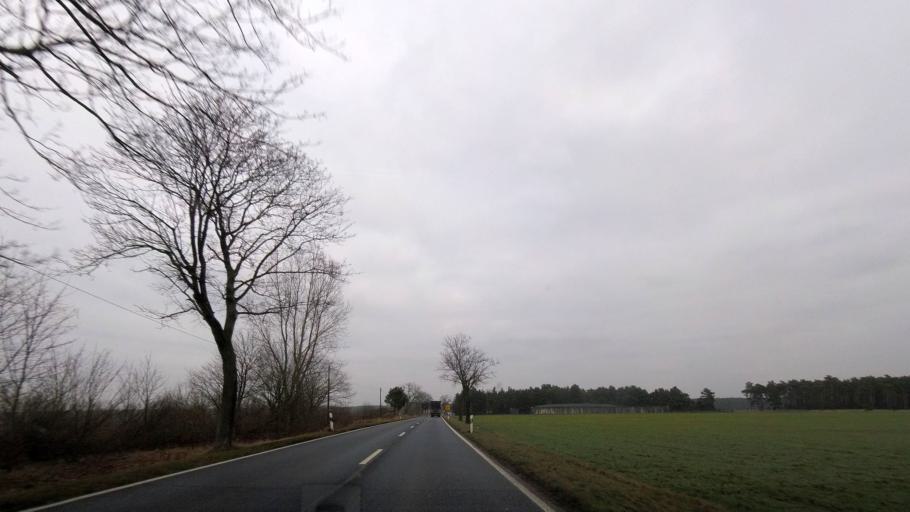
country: DE
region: Brandenburg
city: Beelitz
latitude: 52.1317
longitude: 12.9865
